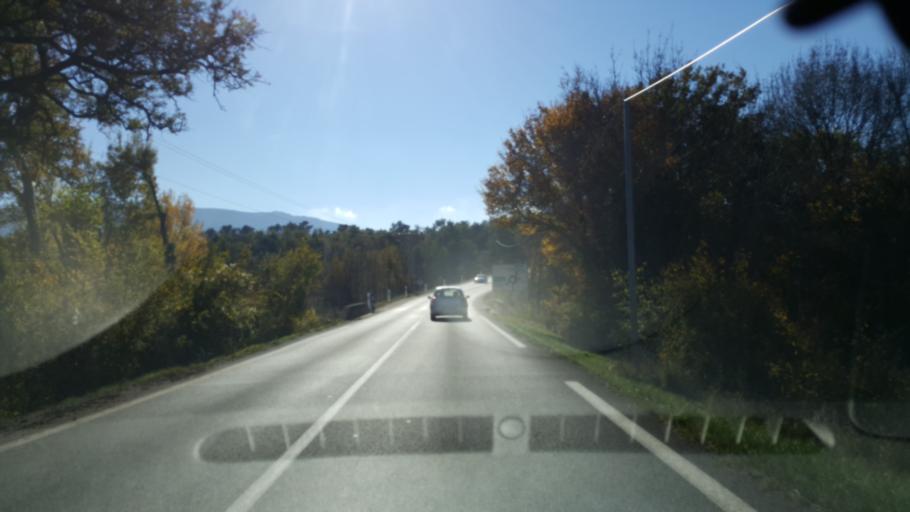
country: FR
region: Provence-Alpes-Cote d'Azur
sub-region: Departement du Var
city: Nans-les-Pins
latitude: 43.3946
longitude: 5.7996
